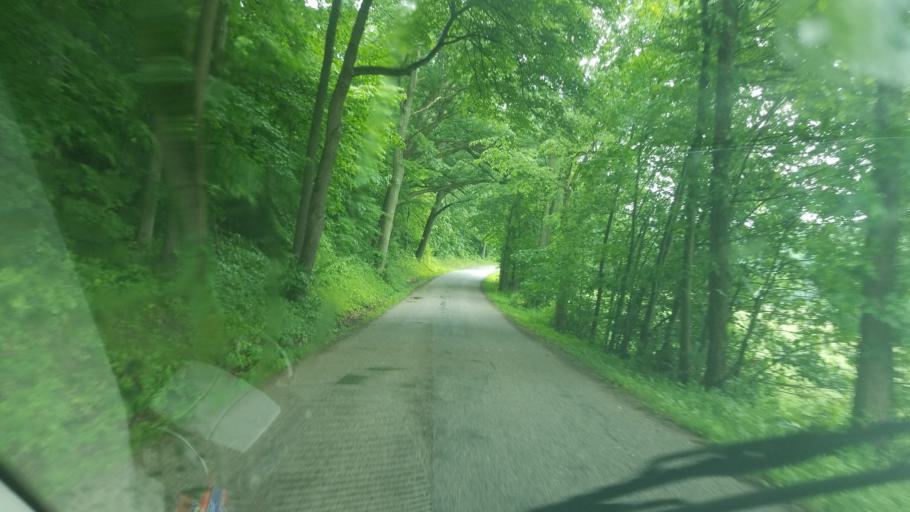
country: US
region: Ohio
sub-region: Sandusky County
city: Bellville
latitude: 40.6146
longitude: -82.4596
